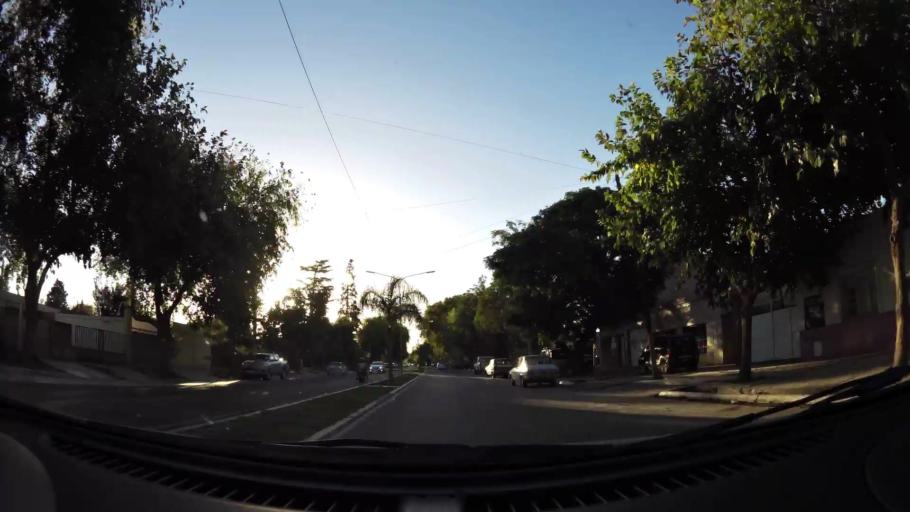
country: AR
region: San Juan
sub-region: Departamento de Santa Lucia
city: Santa Lucia
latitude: -31.5431
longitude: -68.4882
